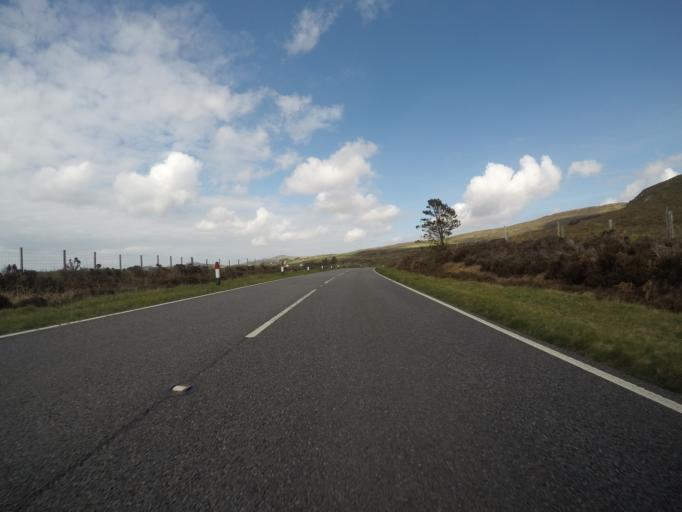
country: GB
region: Scotland
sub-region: Highland
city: Portree
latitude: 57.5549
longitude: -6.3654
